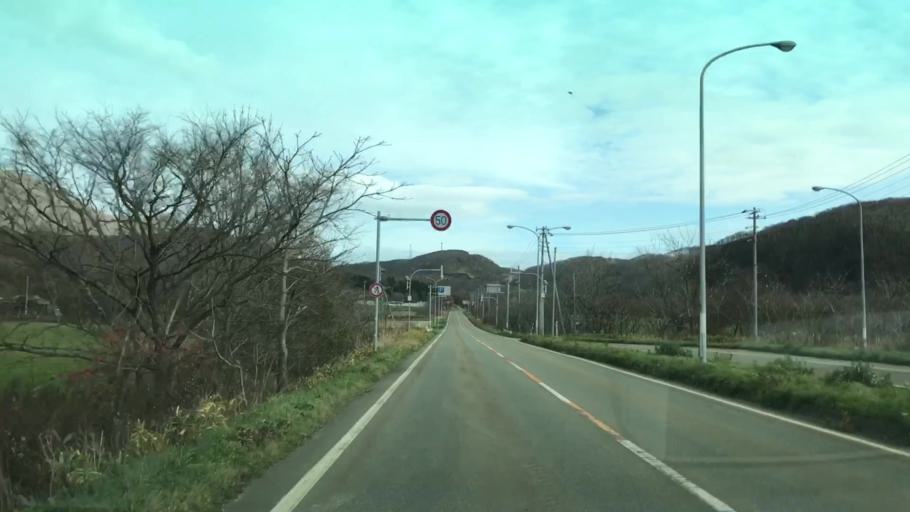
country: JP
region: Hokkaido
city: Obihiro
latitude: 42.0238
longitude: 143.2052
